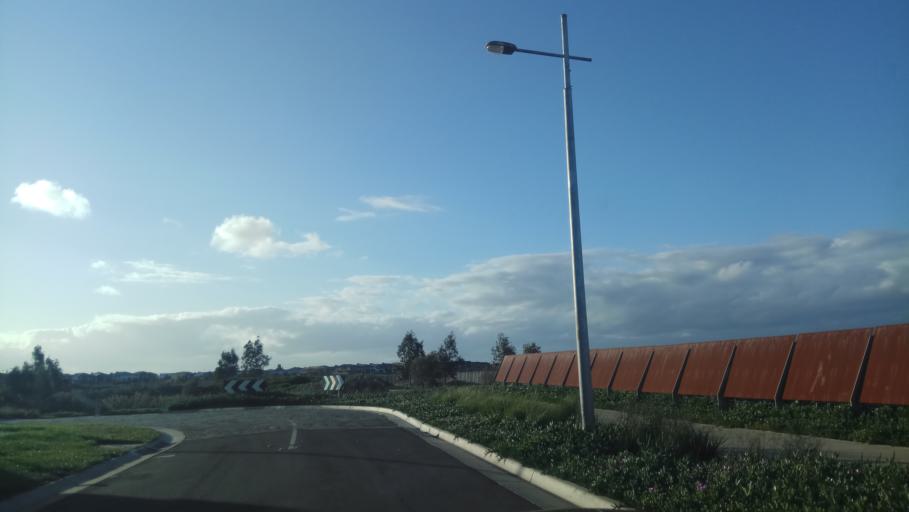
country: AU
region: Victoria
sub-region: Hobsons Bay
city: Altona Meadows
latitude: -37.9111
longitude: 144.7840
